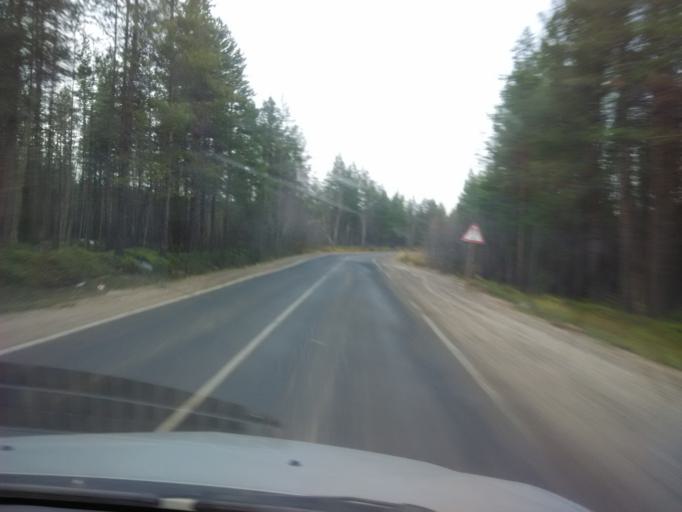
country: RU
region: Murmansk
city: Kandalaksha
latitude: 67.2396
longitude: 32.4109
